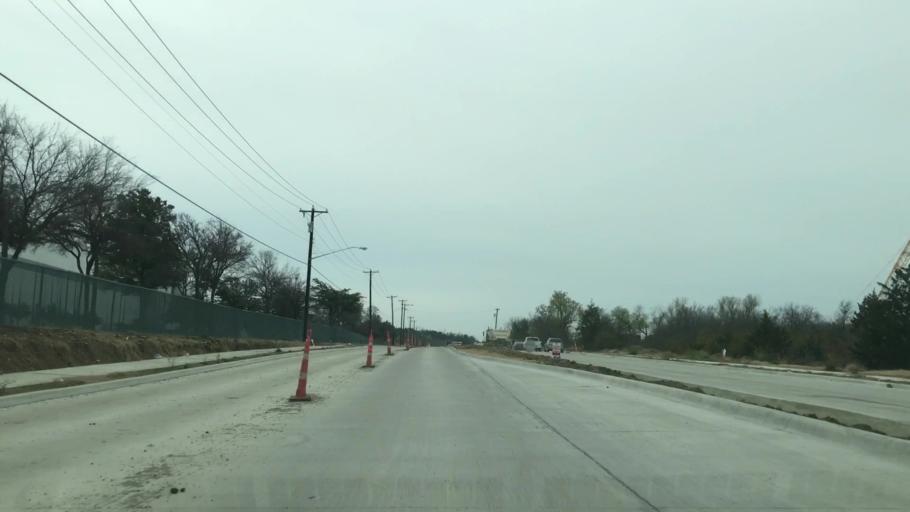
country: US
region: Texas
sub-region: Dallas County
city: Cockrell Hill
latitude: 32.7610
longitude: -96.9022
